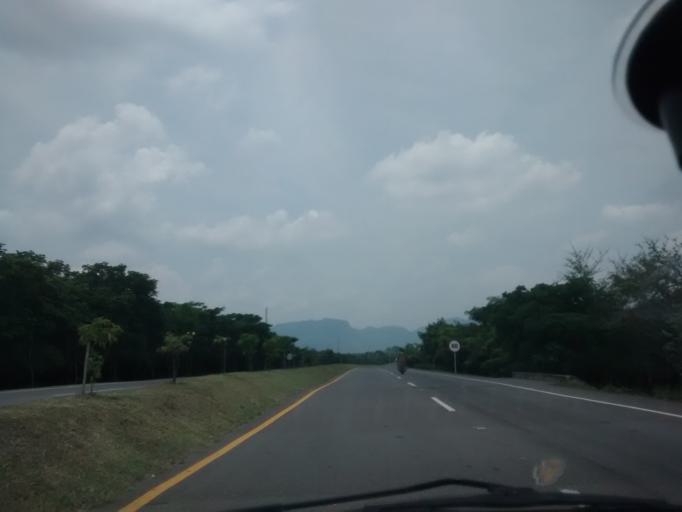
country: CO
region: Tolima
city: Valle de San Juan
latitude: 4.2504
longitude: -74.9849
